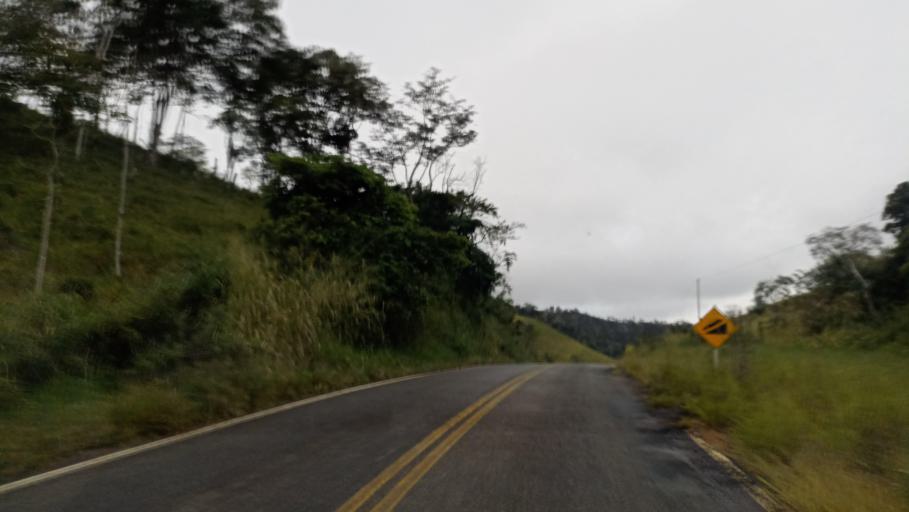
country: BR
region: Bahia
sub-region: Itanhem
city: Itanhem
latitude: -16.6911
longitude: -40.5136
